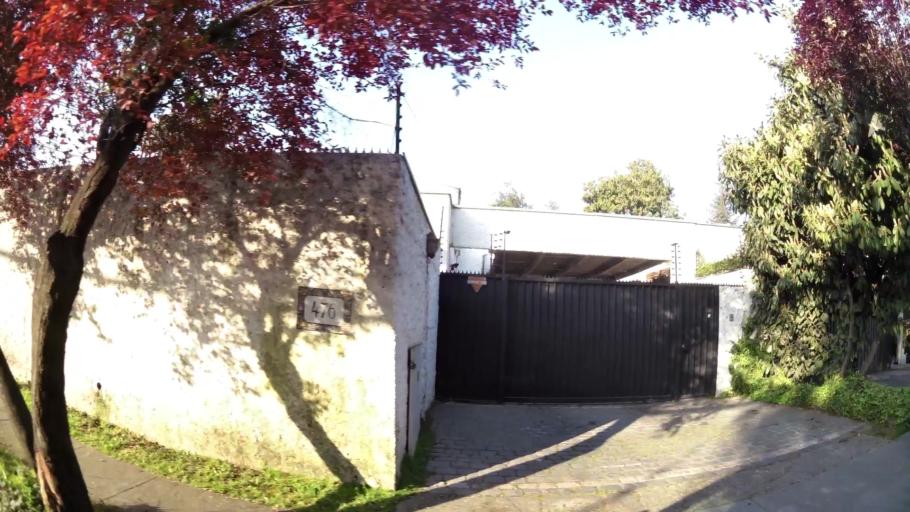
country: CL
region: Santiago Metropolitan
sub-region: Provincia de Santiago
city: Villa Presidente Frei, Nunoa, Santiago, Chile
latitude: -33.3788
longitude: -70.5194
